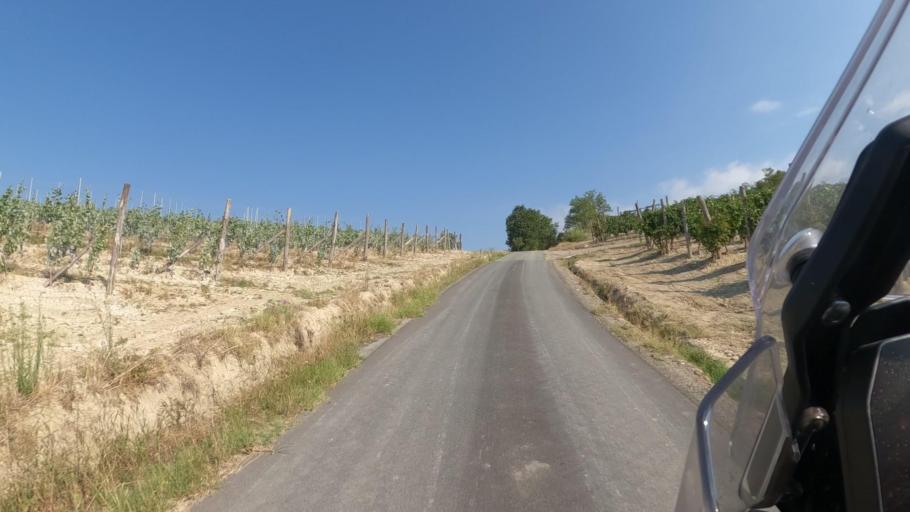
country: IT
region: Piedmont
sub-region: Provincia di Asti
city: Castel Boglione
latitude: 44.7463
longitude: 8.3874
